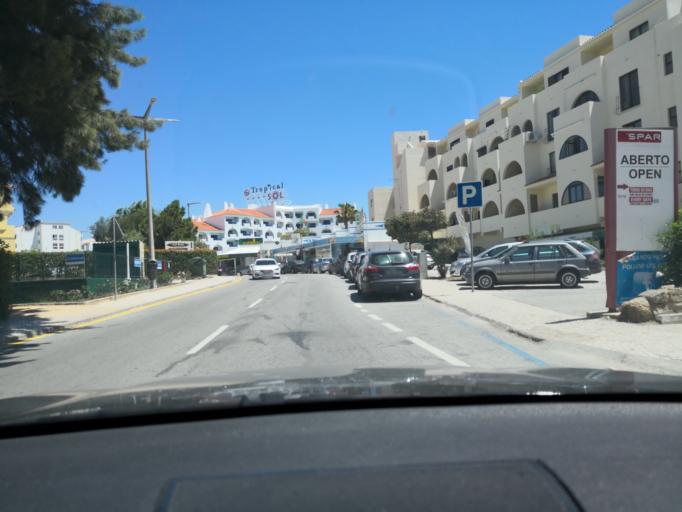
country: PT
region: Faro
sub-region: Albufeira
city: Albufeira
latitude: 37.0916
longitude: -8.2335
